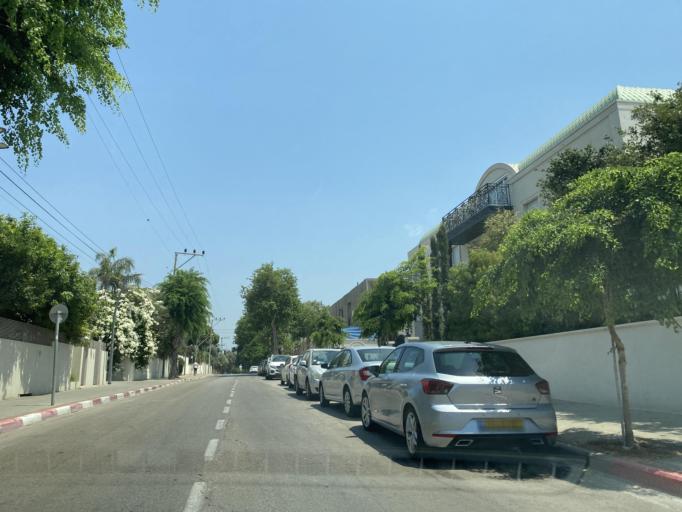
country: IL
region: Tel Aviv
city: Herzliya Pituah
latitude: 32.1786
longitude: 34.8070
